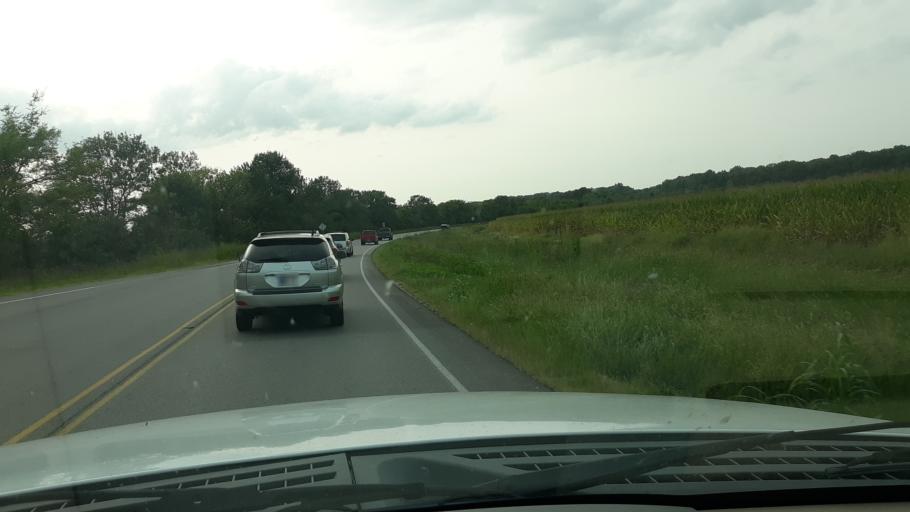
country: US
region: Indiana
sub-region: Gibson County
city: Owensville
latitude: 38.3563
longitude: -87.6892
